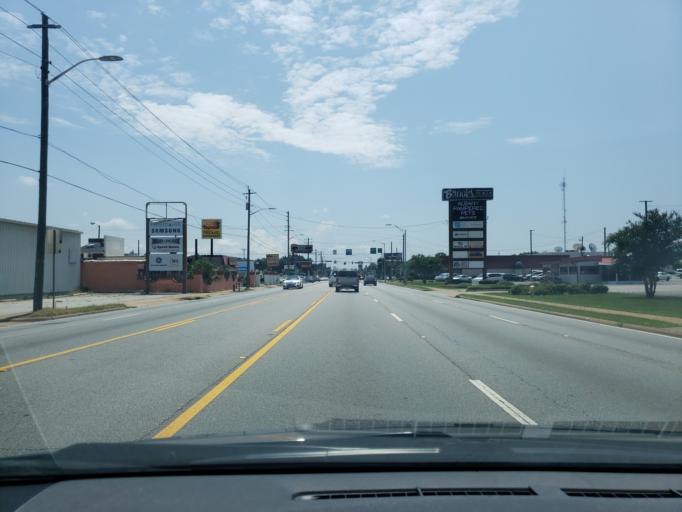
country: US
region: Georgia
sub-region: Dougherty County
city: Albany
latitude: 31.5784
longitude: -84.1762
